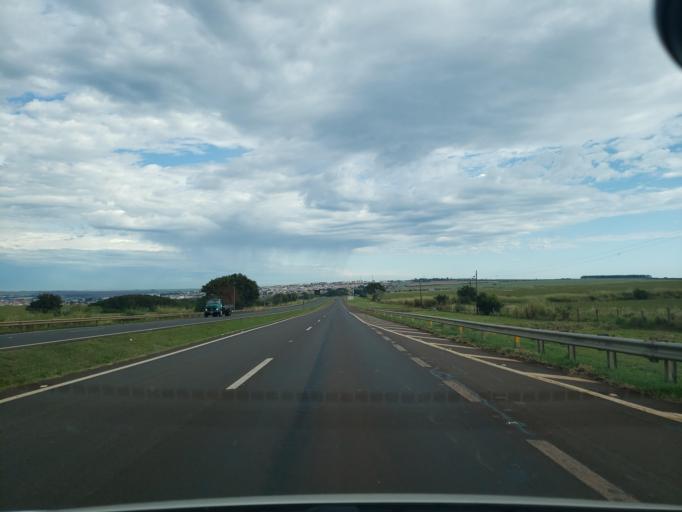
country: BR
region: Sao Paulo
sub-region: Jau
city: Jau
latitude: -22.2651
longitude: -48.5181
